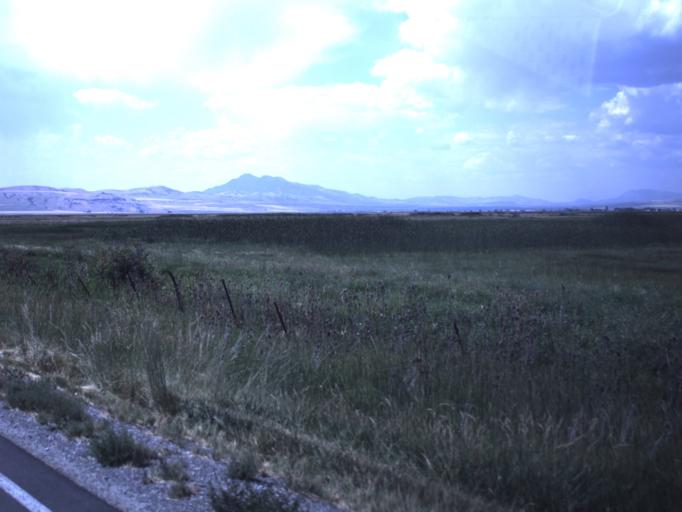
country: US
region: Utah
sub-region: Cache County
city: Benson
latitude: 41.7435
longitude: -111.9193
